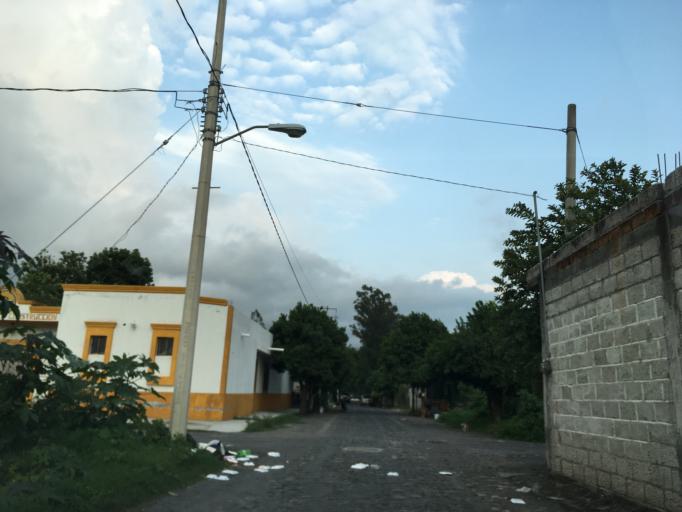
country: MX
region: Nayarit
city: Jala
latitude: 21.1004
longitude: -104.4393
